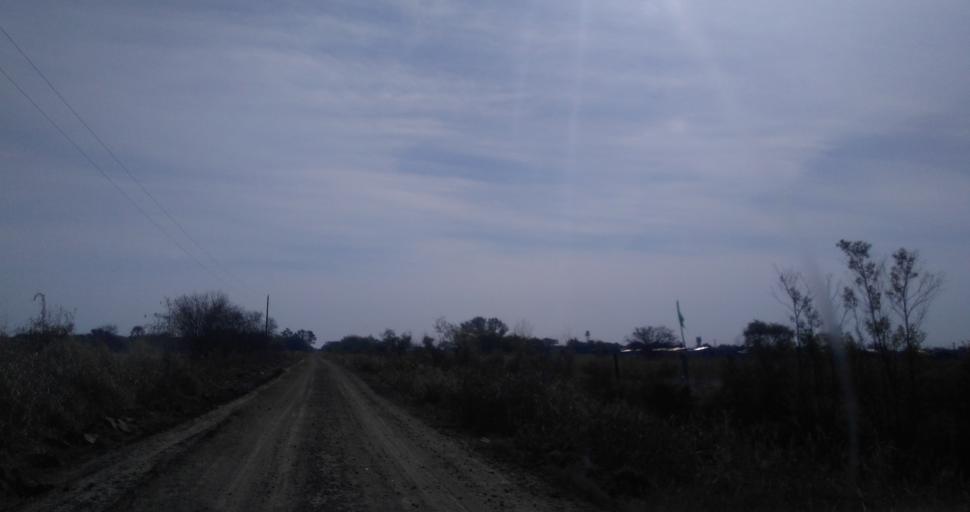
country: AR
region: Chaco
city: Fontana
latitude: -27.4632
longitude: -59.0446
